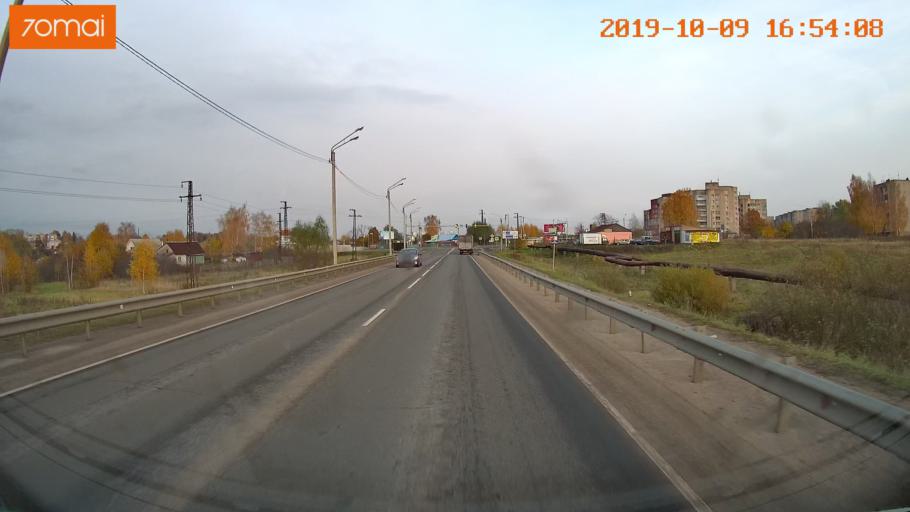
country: RU
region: Ivanovo
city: Privolzhsk
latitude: 57.3759
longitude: 41.2782
